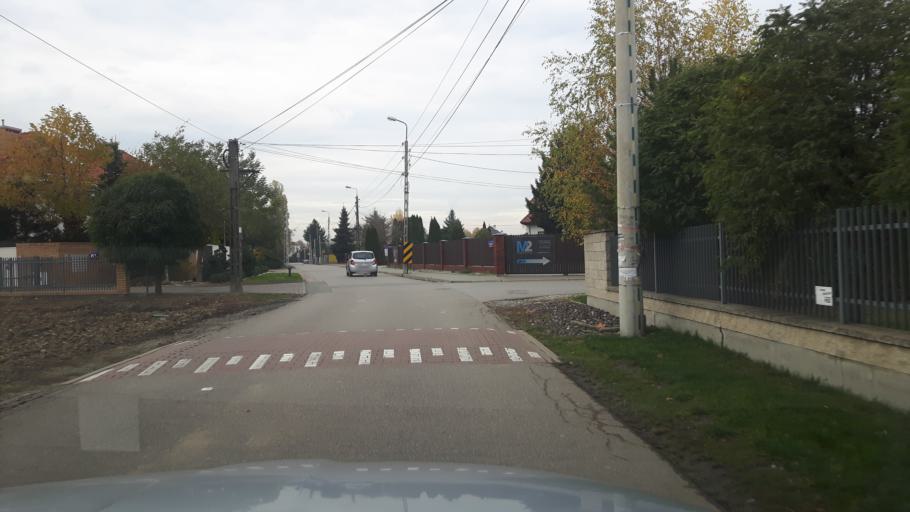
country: PL
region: Masovian Voivodeship
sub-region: Warszawa
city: Wilanow
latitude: 52.1628
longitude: 21.1231
